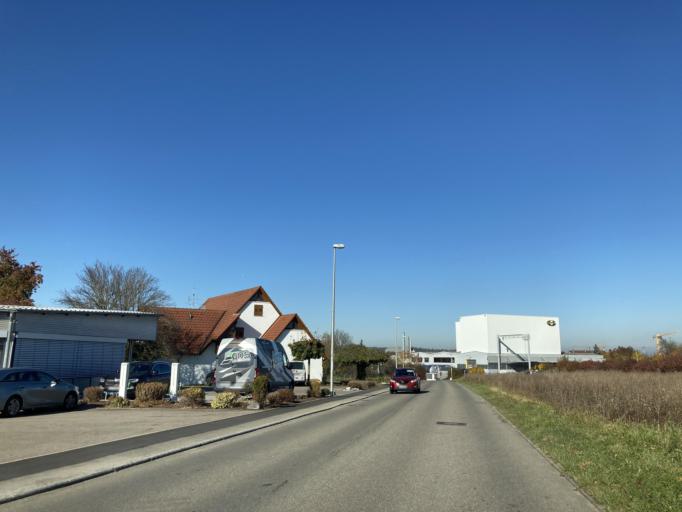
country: DE
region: Baden-Wuerttemberg
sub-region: Tuebingen Region
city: Ofterdingen
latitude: 48.4165
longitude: 9.0393
